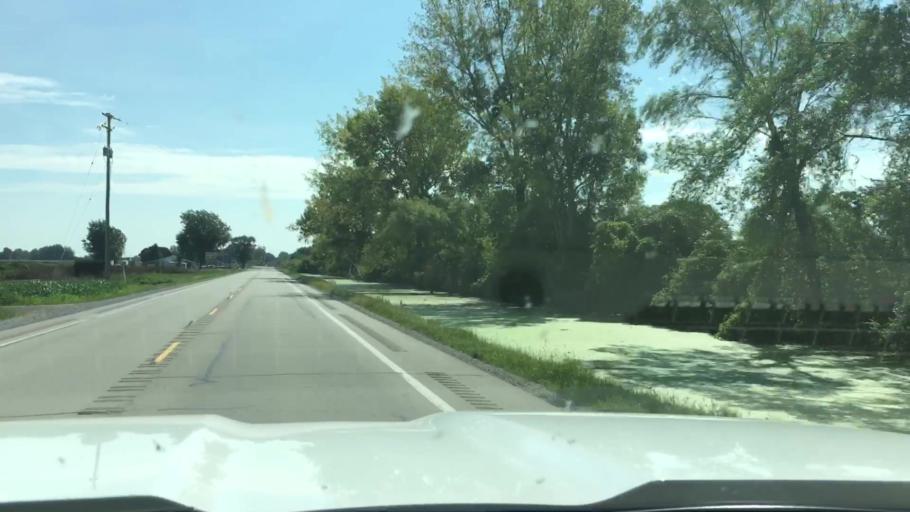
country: US
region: Michigan
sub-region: Tuscola County
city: Reese
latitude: 43.5820
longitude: -83.7067
